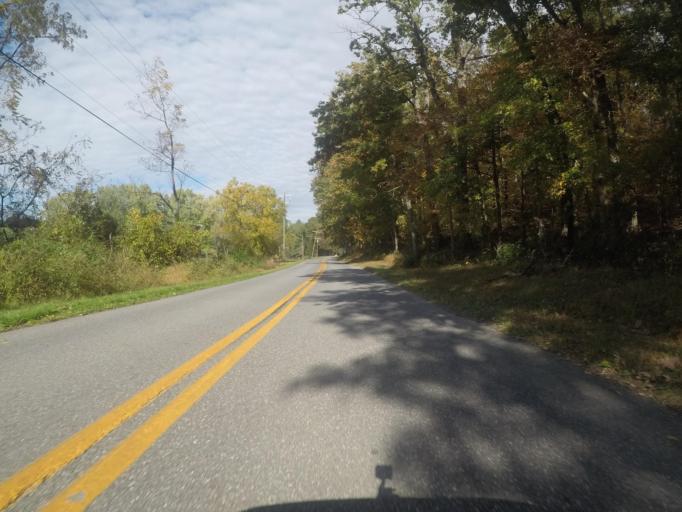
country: US
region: Maryland
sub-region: Carroll County
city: Hampstead
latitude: 39.5673
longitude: -76.8251
